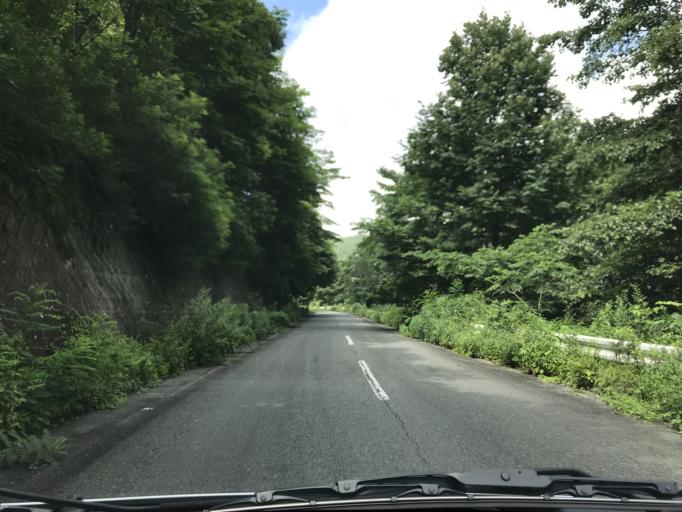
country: JP
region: Iwate
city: Tono
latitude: 39.0884
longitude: 141.4105
